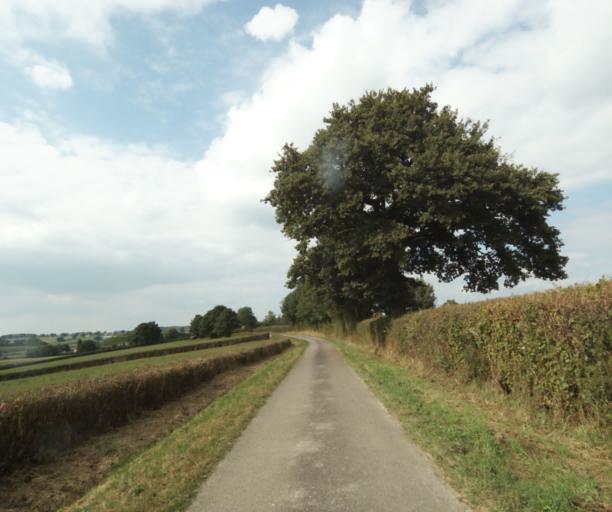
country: FR
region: Bourgogne
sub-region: Departement de Saone-et-Loire
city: Palinges
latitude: 46.5002
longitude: 4.1923
